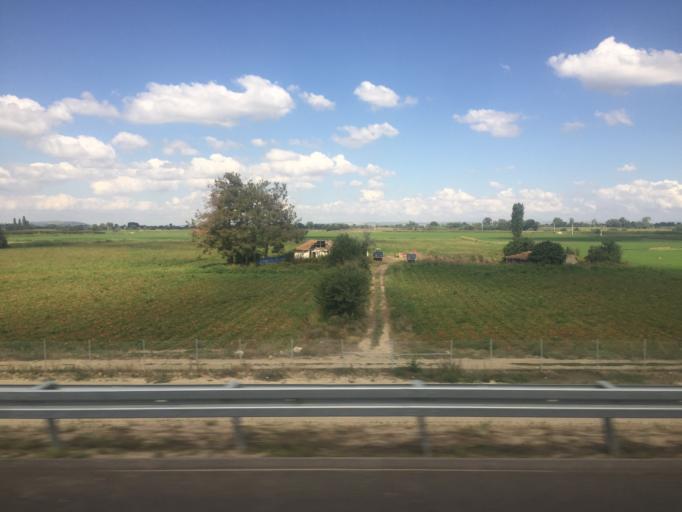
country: TR
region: Bursa
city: Tatkavakli
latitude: 40.0794
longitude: 28.2582
